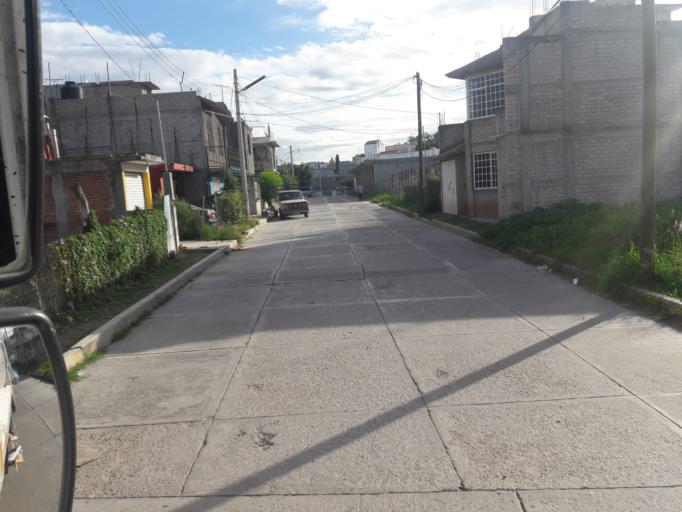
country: MX
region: Oaxaca
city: Ciudad de Huajuapam de Leon
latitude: 17.8045
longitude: -97.7863
